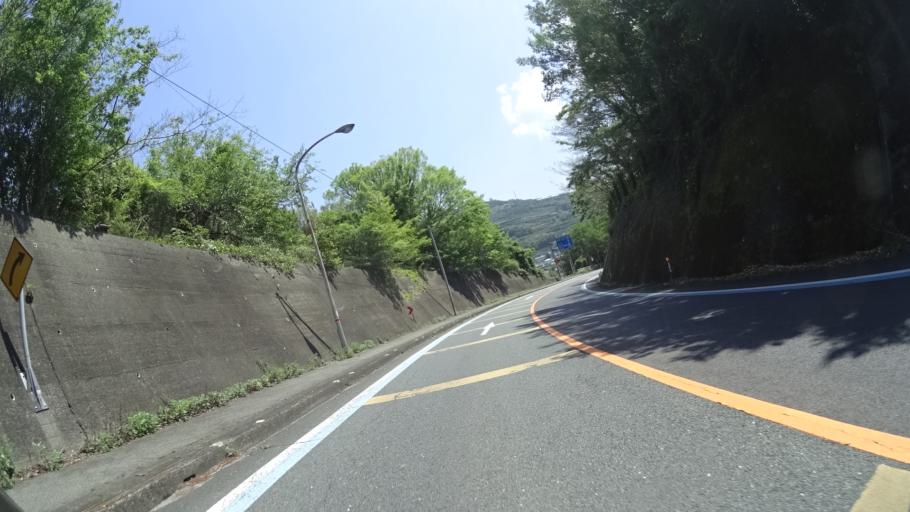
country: JP
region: Ehime
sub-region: Nishiuwa-gun
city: Ikata-cho
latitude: 33.4905
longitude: 132.3935
